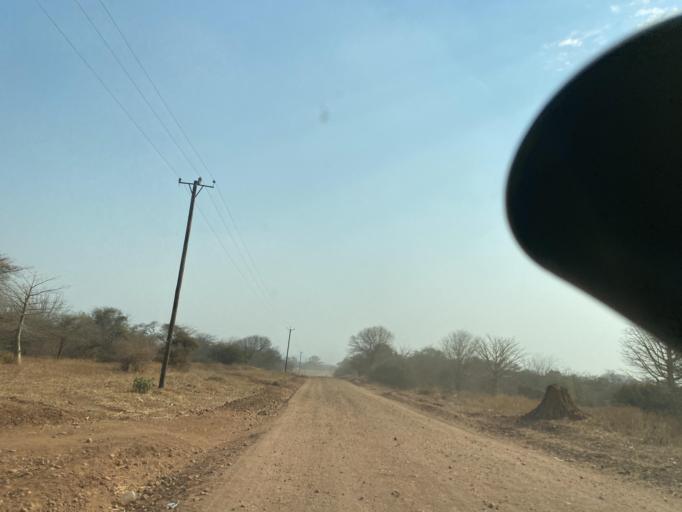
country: ZW
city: Chirundu
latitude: -15.9252
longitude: 28.9716
